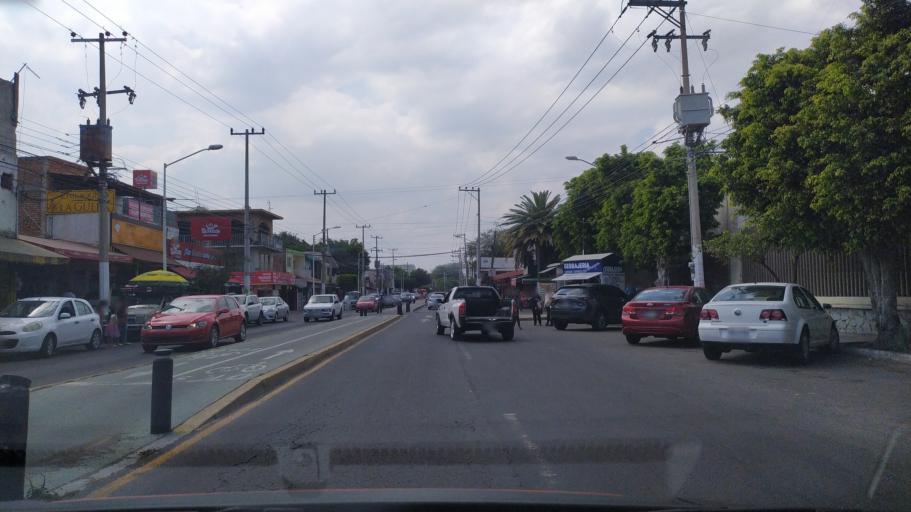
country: MX
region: Jalisco
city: Zapopan2
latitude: 20.7301
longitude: -103.4238
